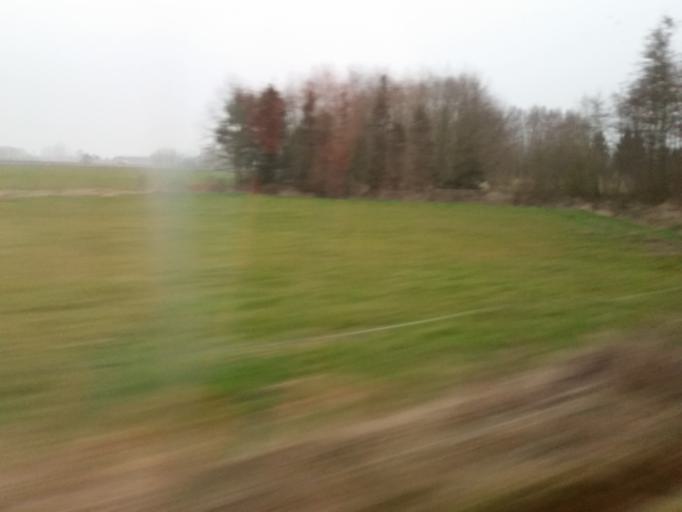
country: BE
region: Flanders
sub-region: Provincie Oost-Vlaanderen
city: Berlare
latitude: 51.0103
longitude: 4.0417
